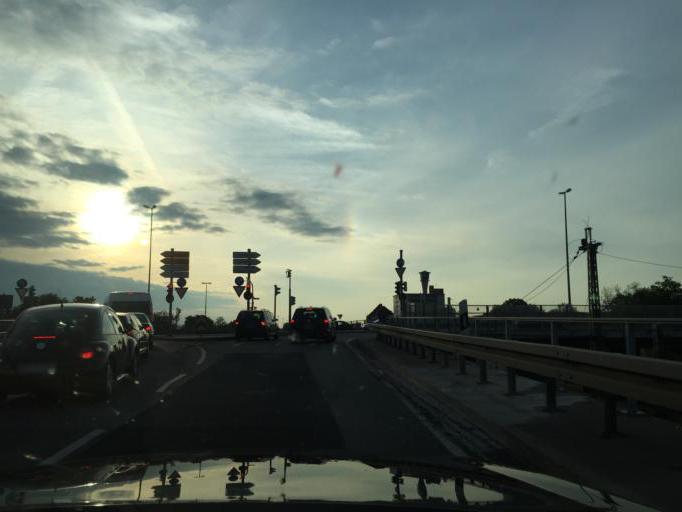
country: DE
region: Bavaria
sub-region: Regierungsbezirk Mittelfranken
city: Wetzendorf
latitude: 49.4514
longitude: 11.0389
